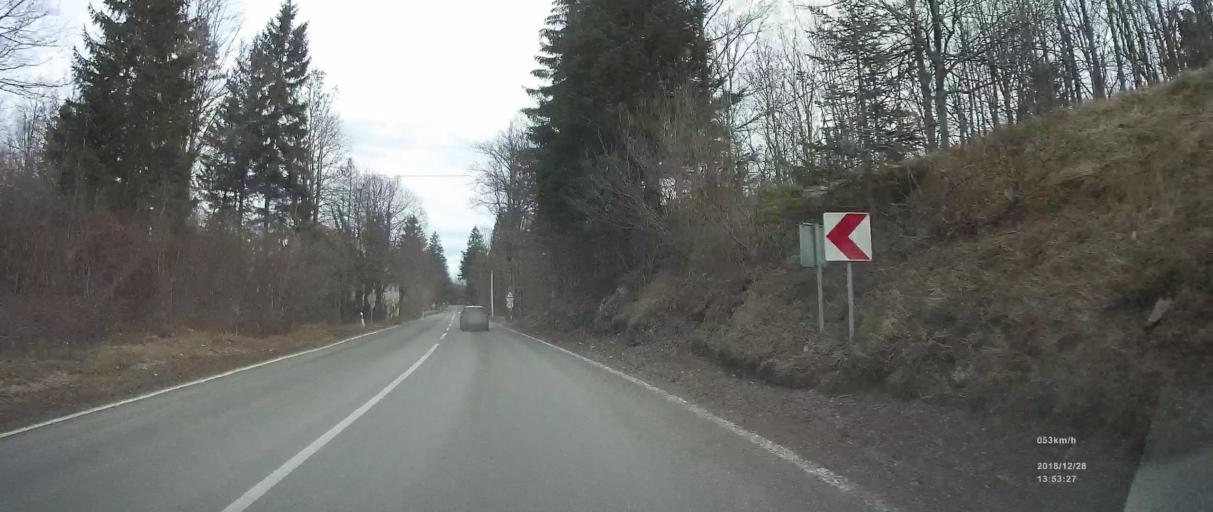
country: HR
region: Primorsko-Goranska
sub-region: Grad Delnice
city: Delnice
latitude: 45.3858
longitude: 14.8526
